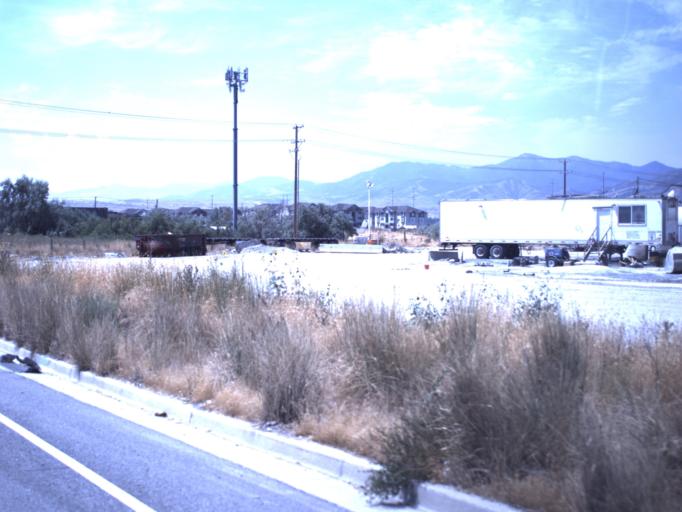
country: US
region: Utah
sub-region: Salt Lake County
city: West Valley City
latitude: 40.7177
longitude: -112.0250
